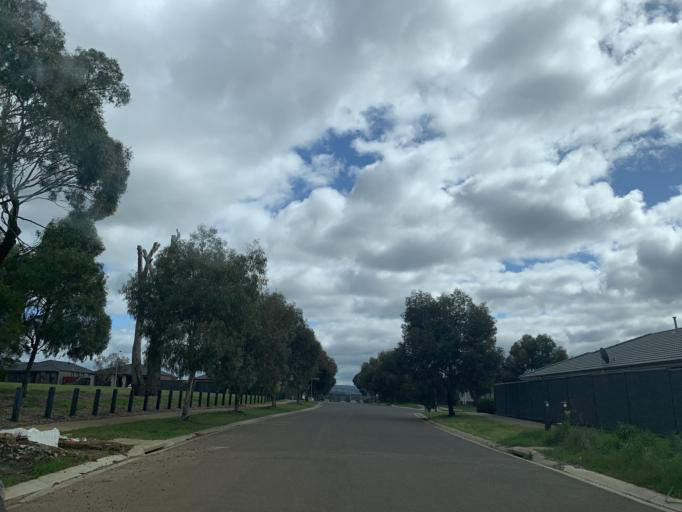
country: AU
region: Victoria
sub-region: Whittlesea
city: Whittlesea
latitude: -37.2902
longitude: 144.9340
